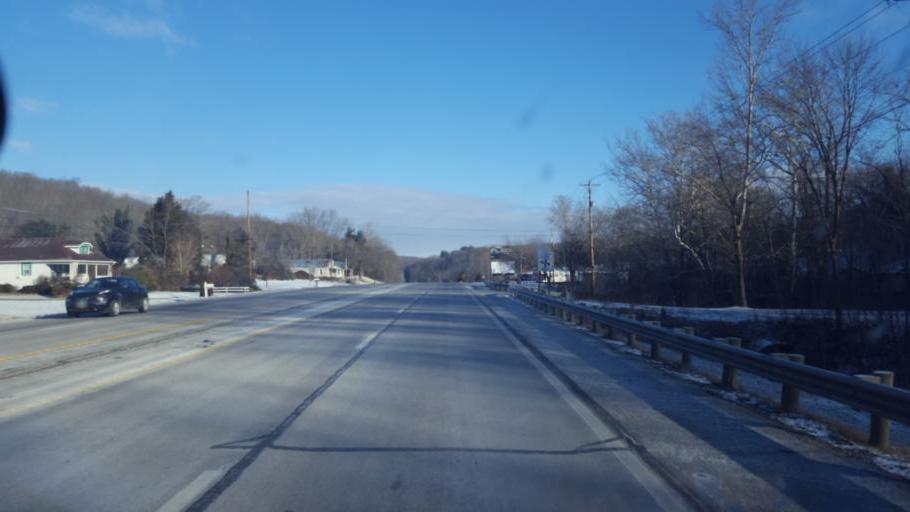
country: US
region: Ohio
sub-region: Ross County
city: Chillicothe
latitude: 39.2369
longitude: -82.9841
